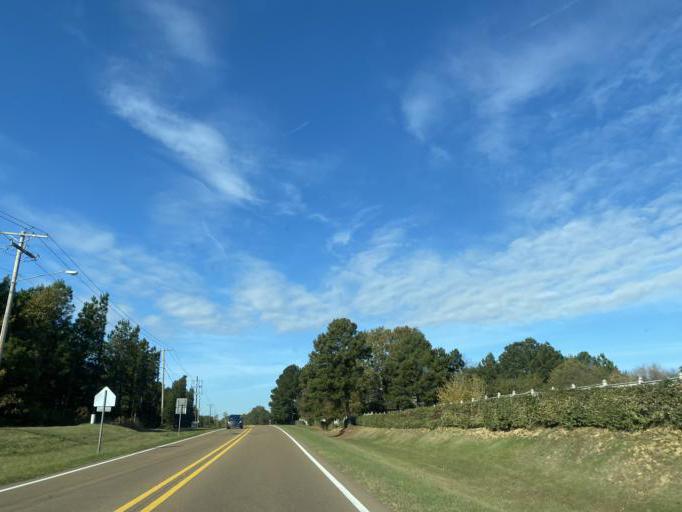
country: US
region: Mississippi
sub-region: Madison County
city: Madison
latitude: 32.4812
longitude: -90.1681
